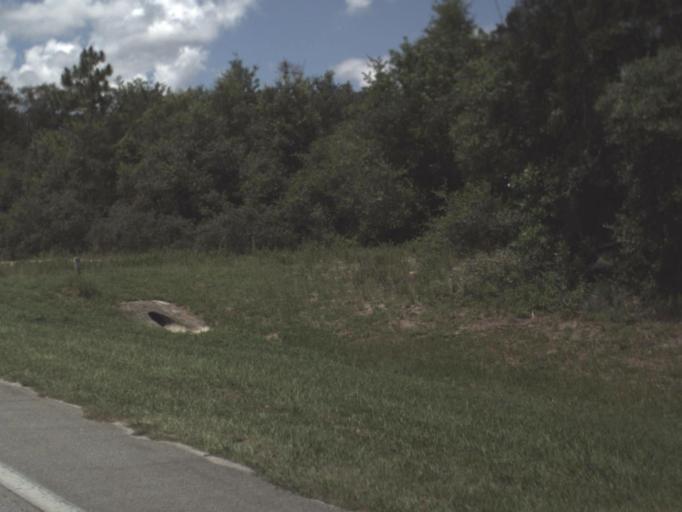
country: US
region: Florida
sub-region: Putnam County
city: Crescent City
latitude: 29.4038
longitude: -81.5094
